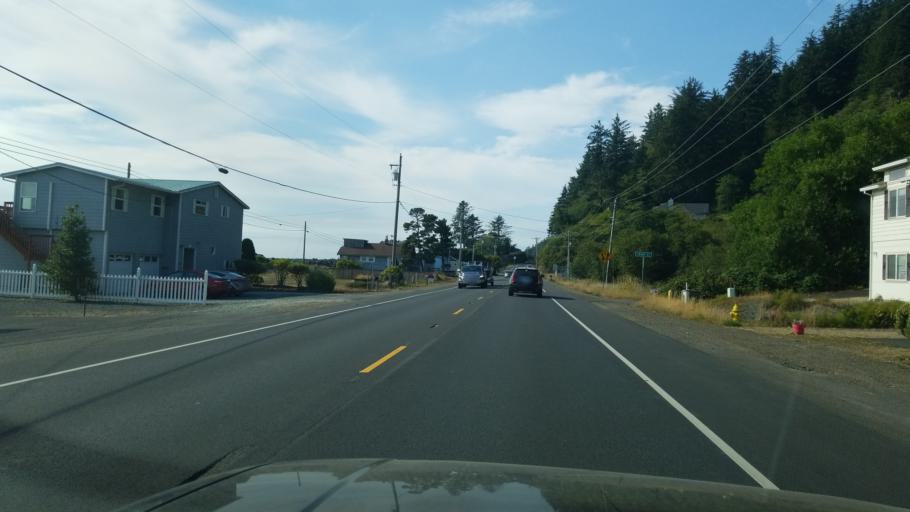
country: US
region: Oregon
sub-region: Tillamook County
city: Rockaway Beach
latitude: 45.5651
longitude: -123.9375
